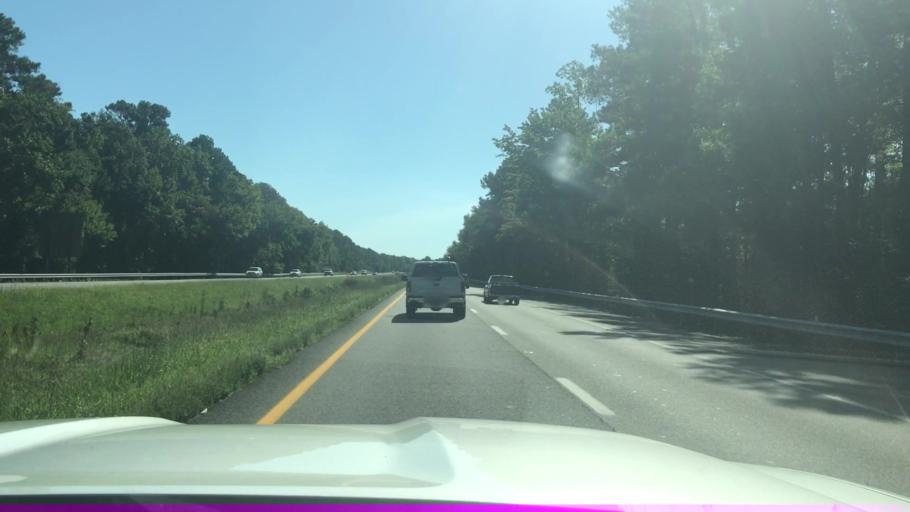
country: US
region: Virginia
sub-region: Henrico County
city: Sandston
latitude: 37.5276
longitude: -77.3003
